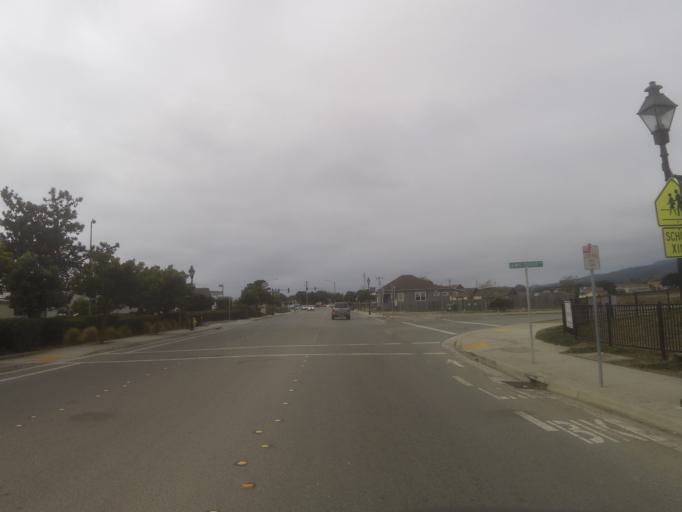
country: US
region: California
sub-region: San Mateo County
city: Half Moon Bay
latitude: 37.4694
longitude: -122.4317
